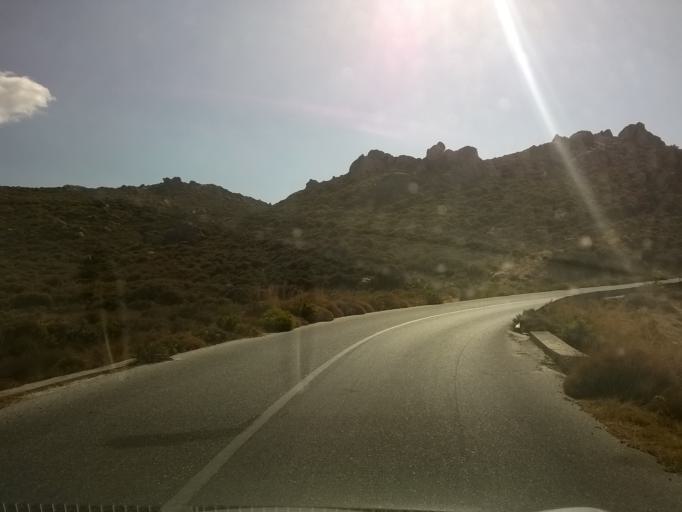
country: GR
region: South Aegean
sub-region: Nomos Kykladon
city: Filotion
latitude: 37.1013
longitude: 25.4856
